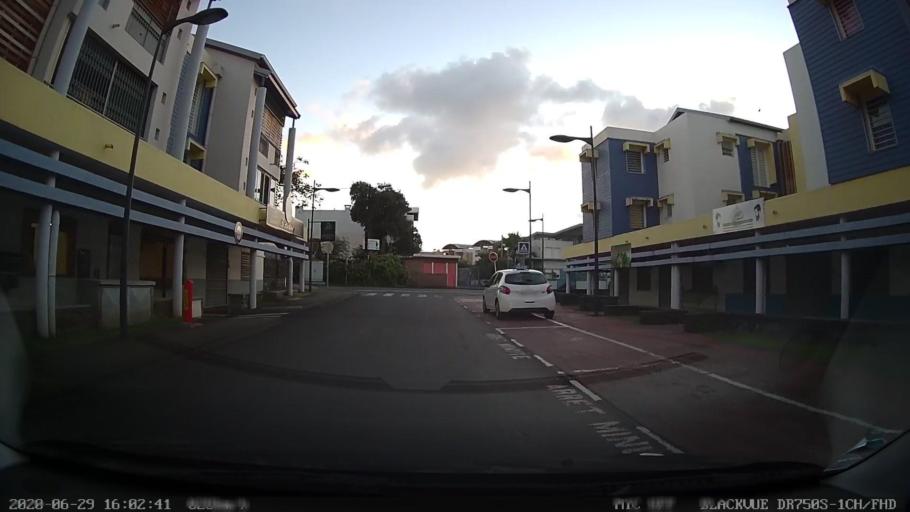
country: RE
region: Reunion
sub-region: Reunion
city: Bras-Panon
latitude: -20.9934
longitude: 55.6778
